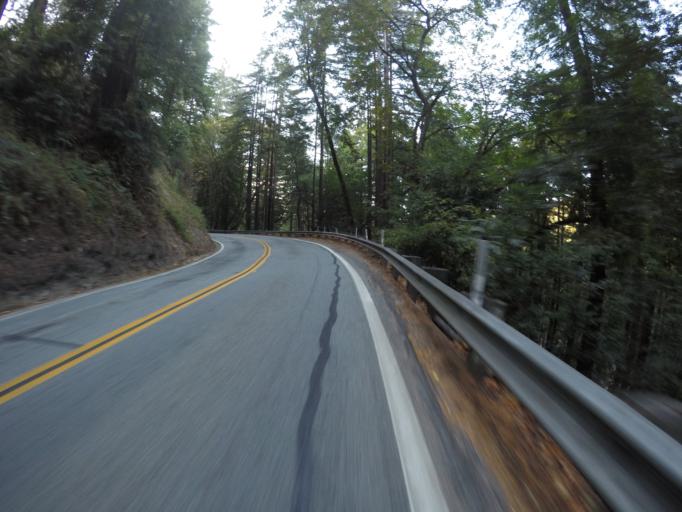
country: US
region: California
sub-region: Santa Cruz County
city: Pasatiempo
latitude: 37.0064
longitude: -122.0431
